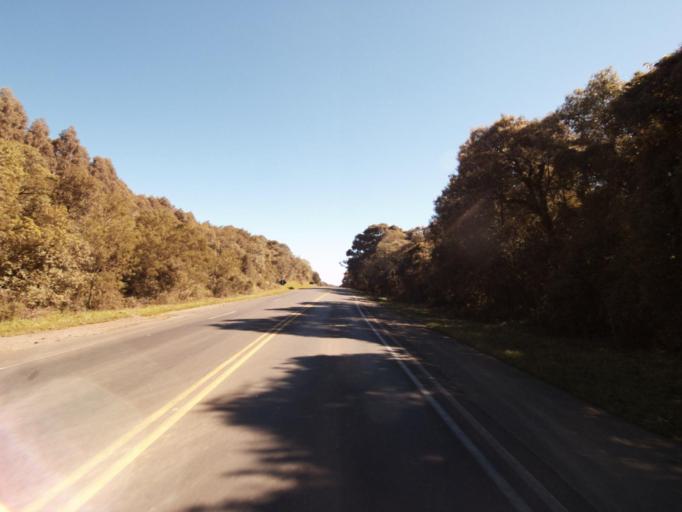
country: BR
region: Santa Catarina
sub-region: Concordia
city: Concordia
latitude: -26.9729
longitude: -51.8438
